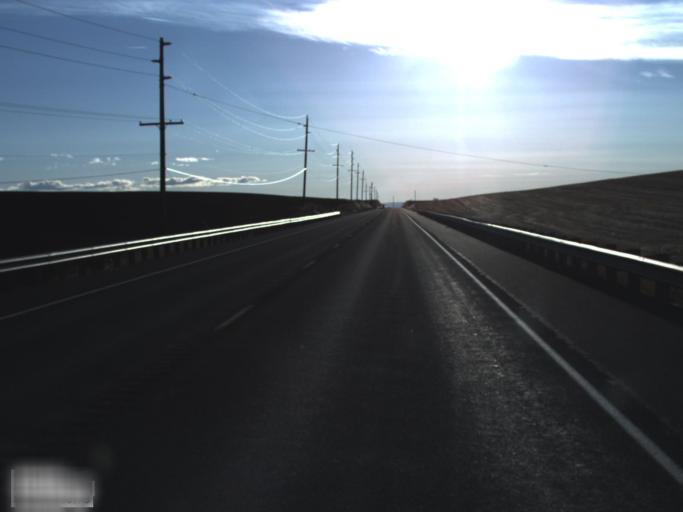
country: US
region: Washington
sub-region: Walla Walla County
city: Walla Walla East
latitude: 46.1121
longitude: -118.2275
